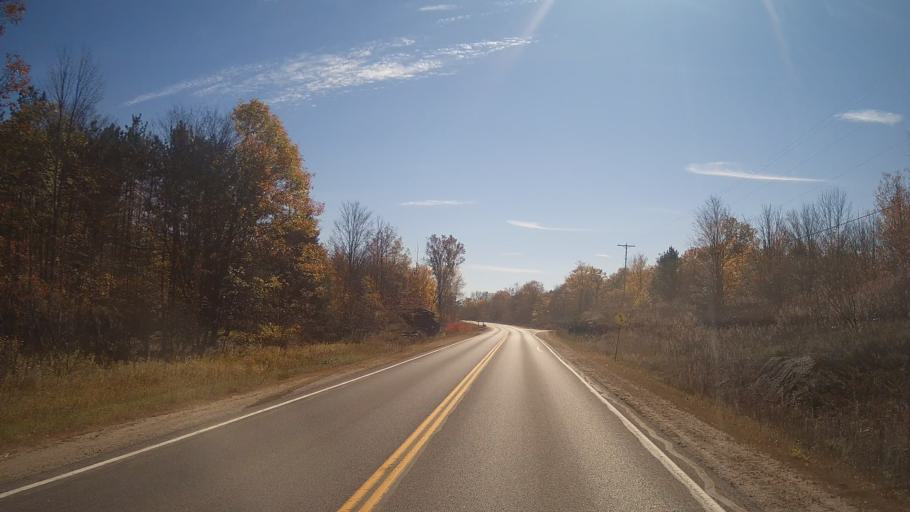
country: CA
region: Ontario
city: Perth
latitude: 44.6981
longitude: -76.6755
